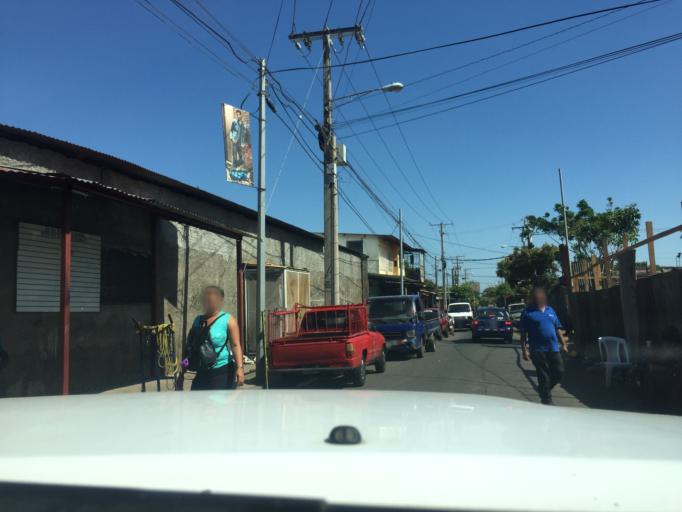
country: NI
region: Managua
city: Managua
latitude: 12.1512
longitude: -86.2569
